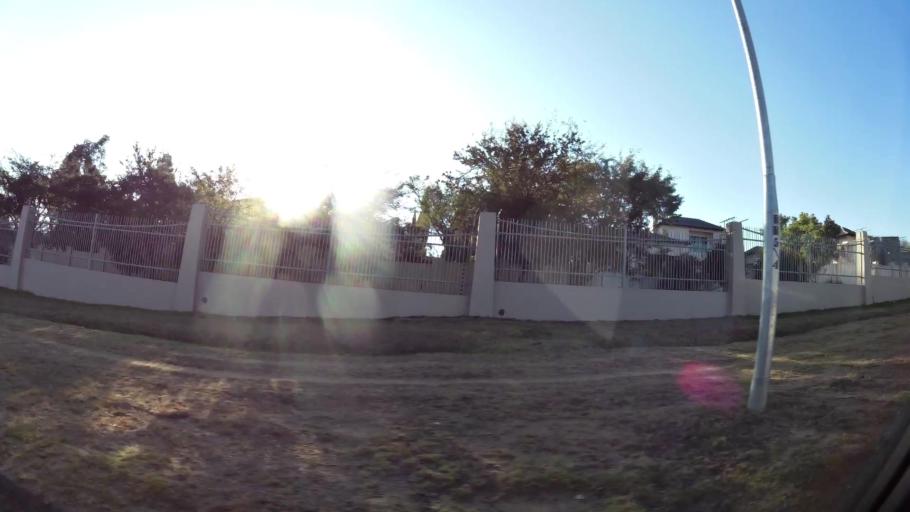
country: ZA
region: Gauteng
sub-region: City of Johannesburg Metropolitan Municipality
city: Midrand
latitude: -25.9770
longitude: 28.1004
